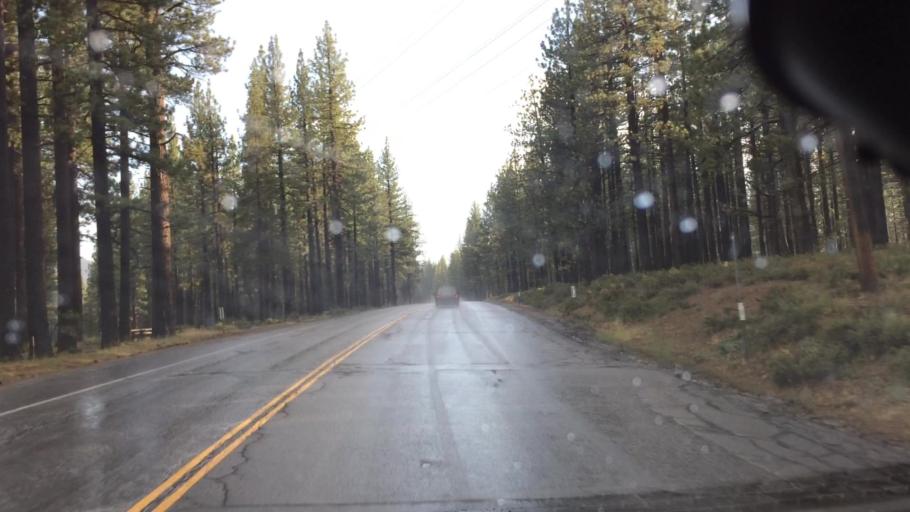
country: US
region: California
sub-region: El Dorado County
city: South Lake Tahoe
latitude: 38.8969
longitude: -119.9708
